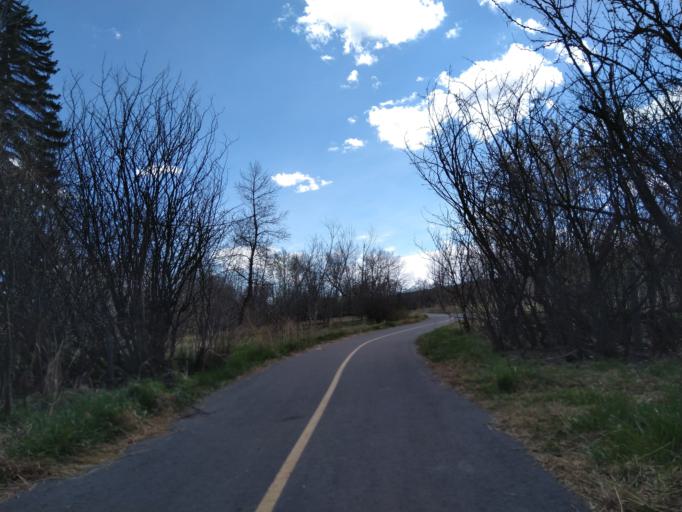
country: CA
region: Alberta
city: Calgary
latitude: 51.0741
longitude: -114.1732
